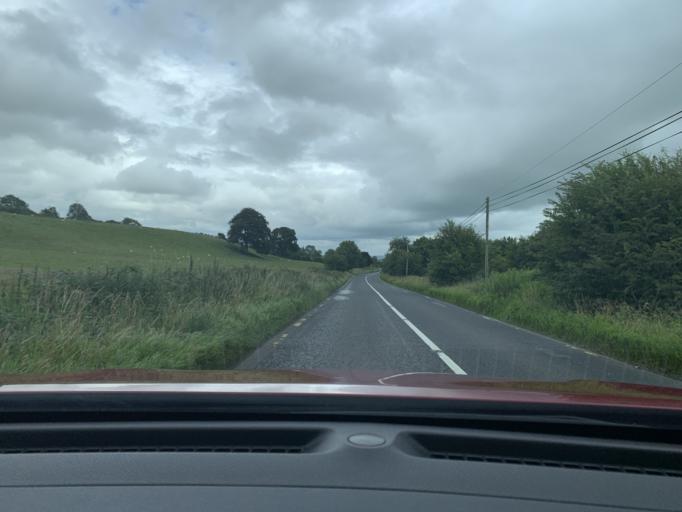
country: IE
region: Ulster
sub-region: County Donegal
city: Convoy
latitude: 54.8007
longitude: -7.6303
